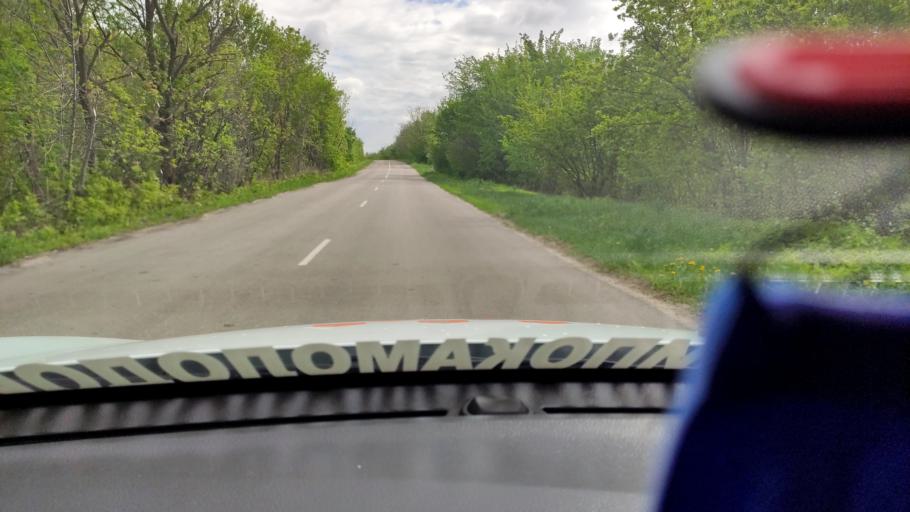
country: RU
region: Voronezj
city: Imeni Pervogo Maya
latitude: 50.6800
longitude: 39.4952
